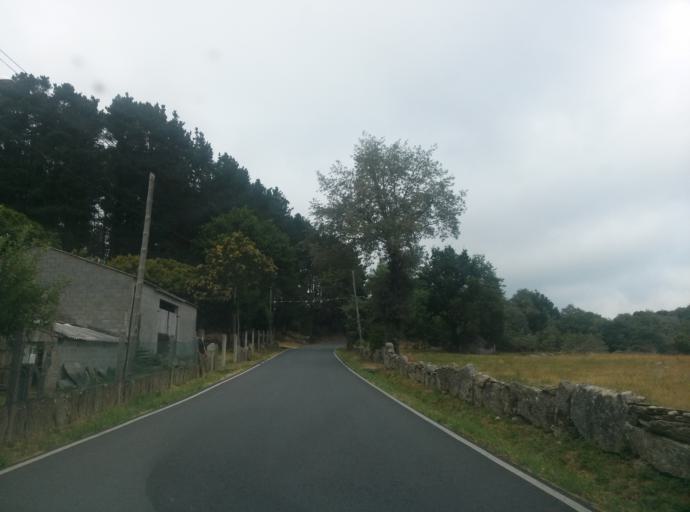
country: ES
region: Galicia
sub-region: Provincia de Lugo
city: Lugo
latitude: 43.0700
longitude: -7.5570
